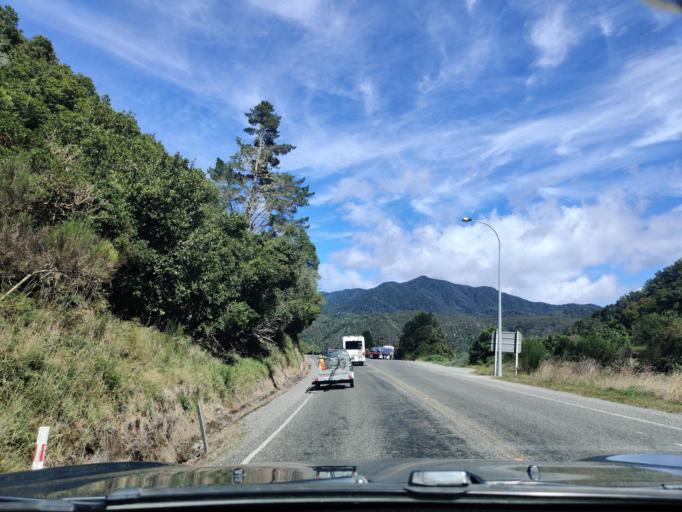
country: NZ
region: West Coast
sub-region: Buller District
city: Westport
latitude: -41.7768
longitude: 172.2204
